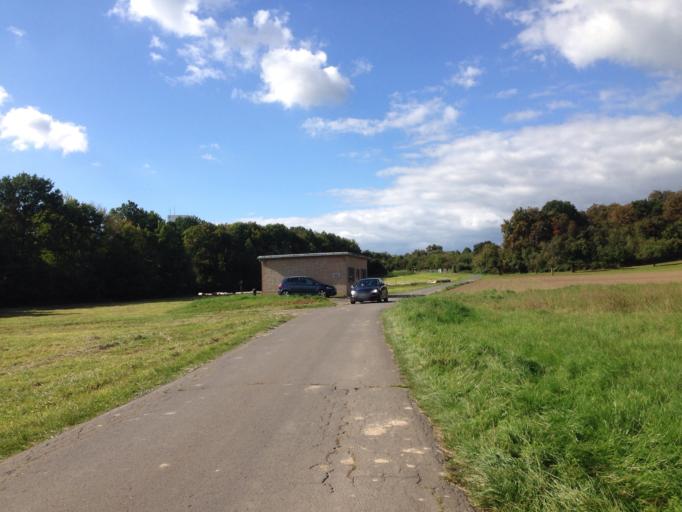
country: DE
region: Hesse
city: Lollar
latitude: 50.6148
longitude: 8.7123
